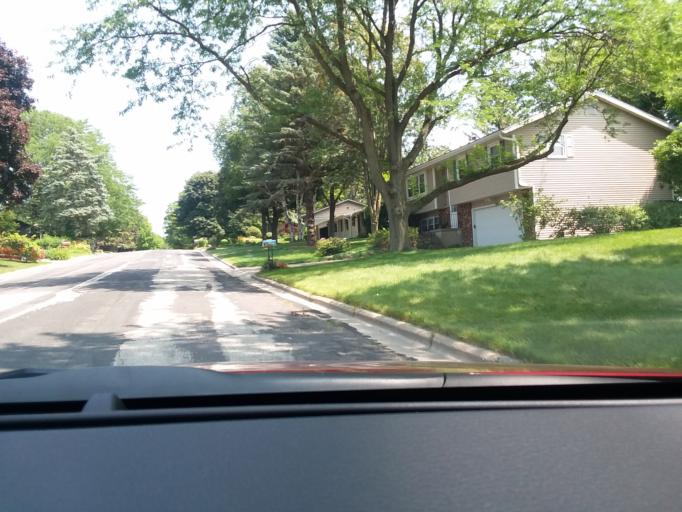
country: US
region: Wisconsin
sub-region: Dane County
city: Shorewood Hills
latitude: 43.0266
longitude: -89.4554
